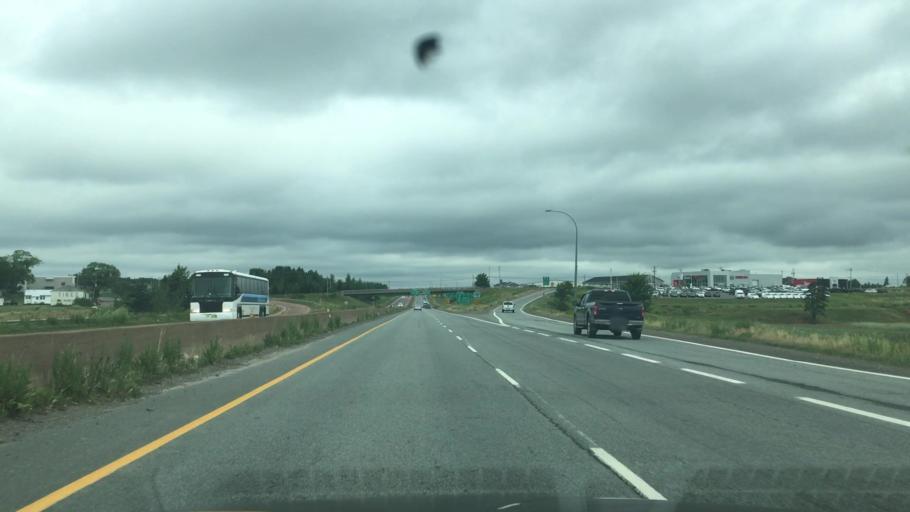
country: CA
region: Nova Scotia
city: Truro
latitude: 45.3763
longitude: -63.3202
